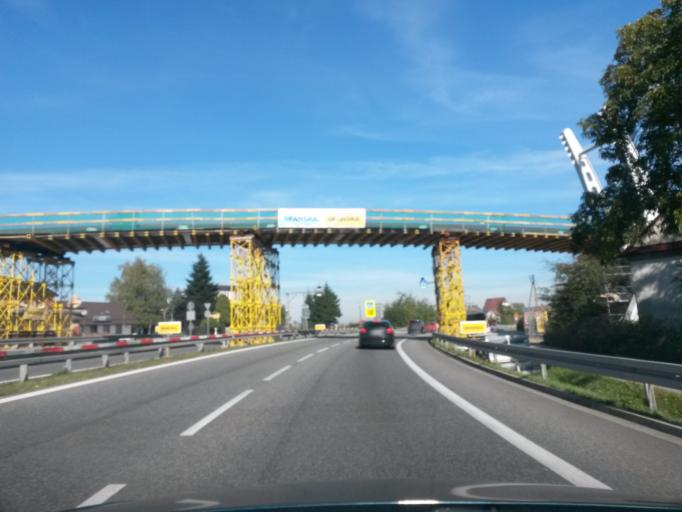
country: PL
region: Lesser Poland Voivodeship
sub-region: Powiat krakowski
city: Libertow
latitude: 49.9592
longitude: 19.8887
